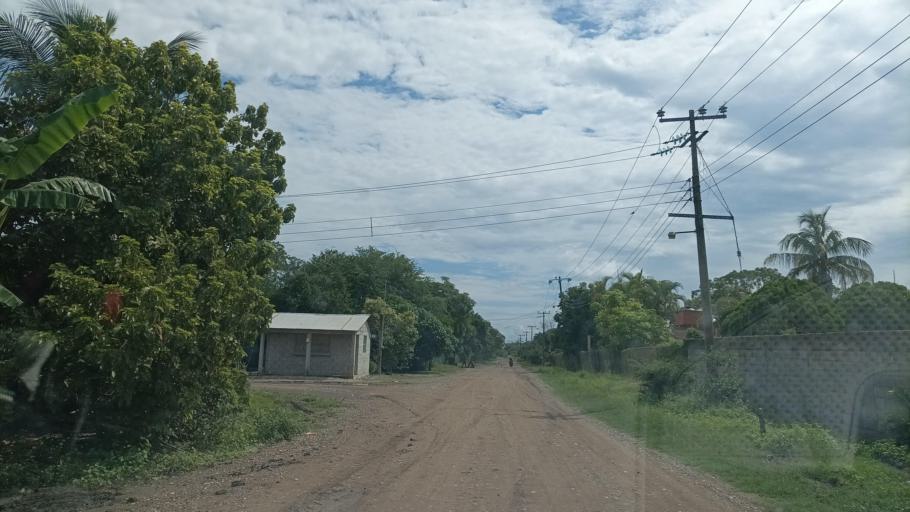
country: MX
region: Veracruz
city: Panuco
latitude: 21.9471
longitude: -98.1369
